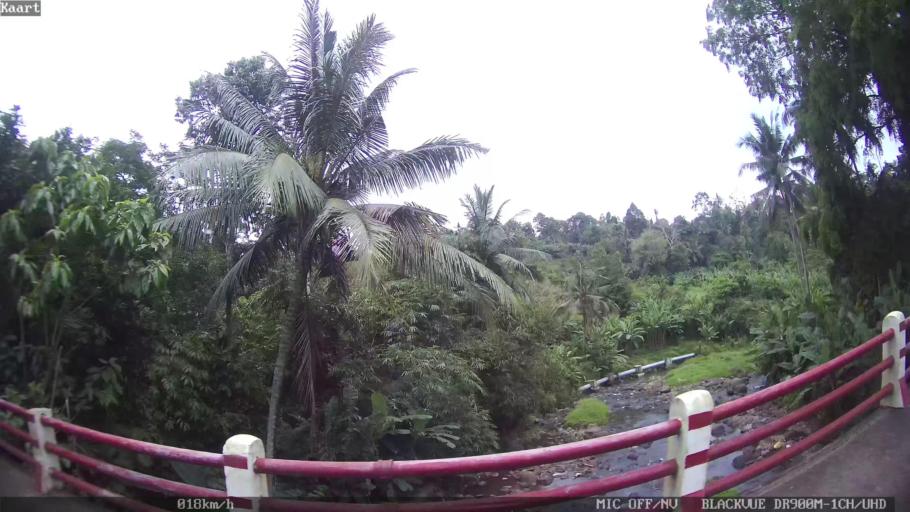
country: ID
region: Lampung
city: Bandarlampung
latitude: -5.4359
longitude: 105.2357
